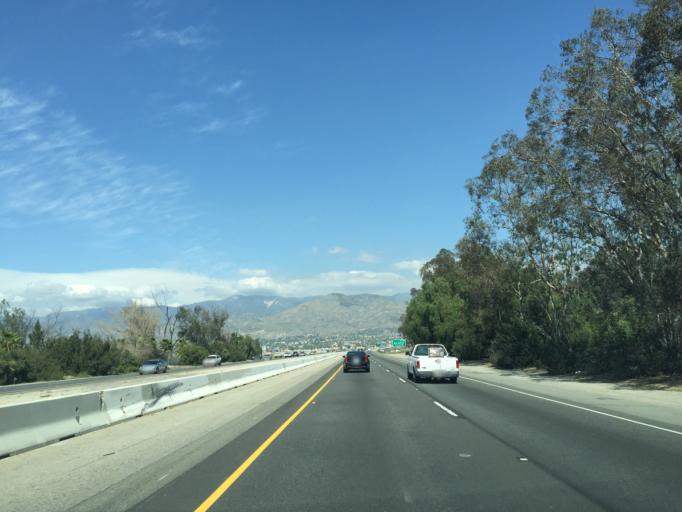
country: US
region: California
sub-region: San Bernardino County
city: Redlands
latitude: 34.0889
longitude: -117.2006
